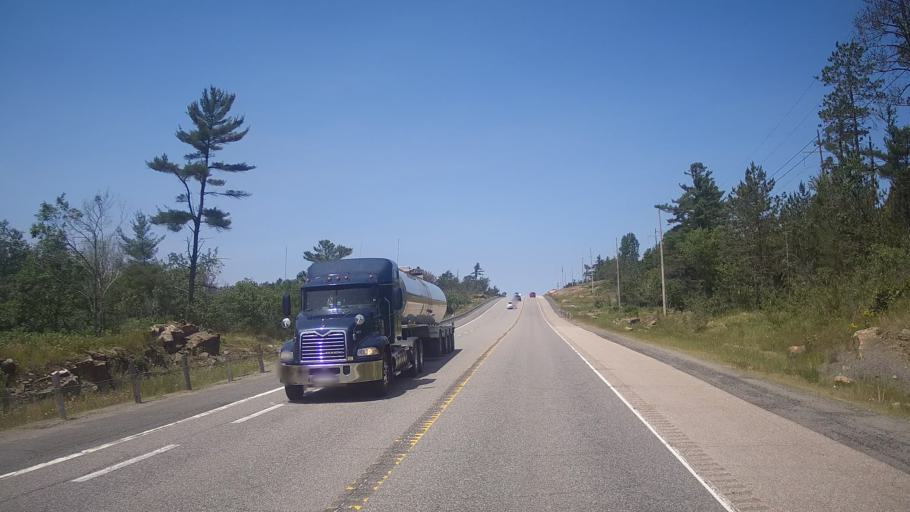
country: CA
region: Ontario
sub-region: Parry Sound District
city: Parry Sound
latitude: 45.6551
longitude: -80.4082
